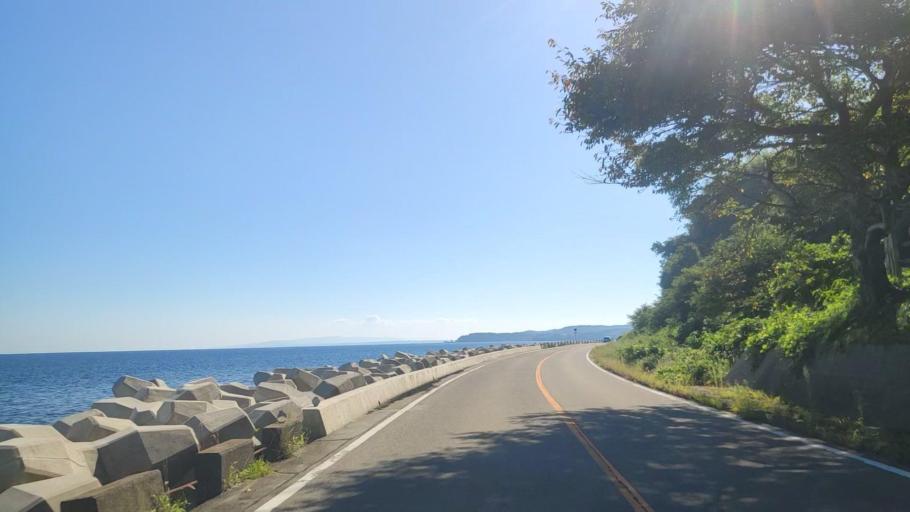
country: JP
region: Ishikawa
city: Nanao
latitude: 37.2871
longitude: 137.1151
